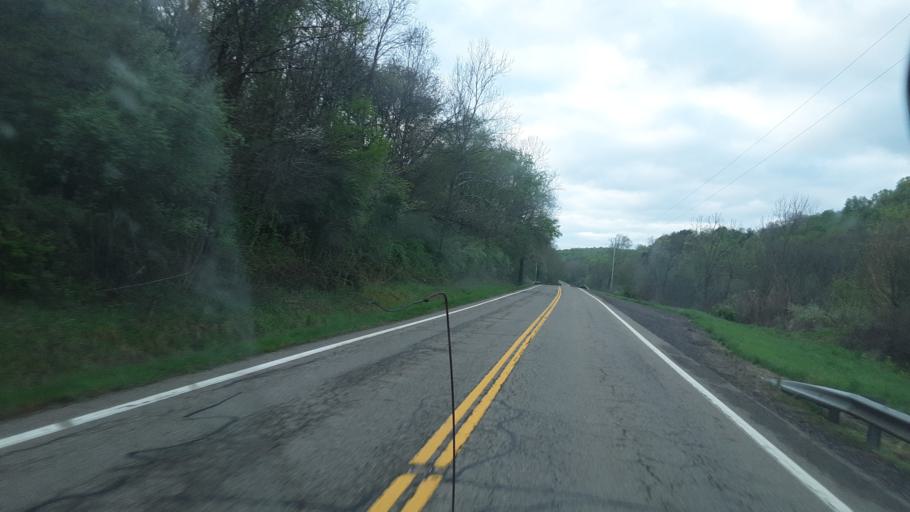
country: US
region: Ohio
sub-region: Coshocton County
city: Coshocton
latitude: 40.1745
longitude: -81.8231
